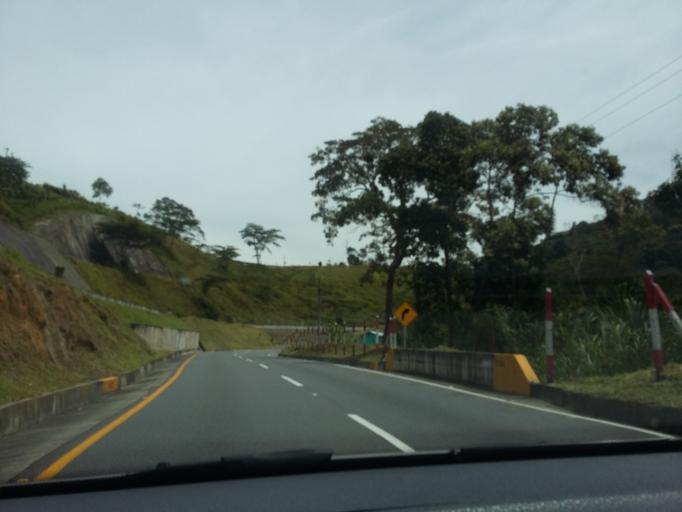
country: CO
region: Santander
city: Bucaramanga
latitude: 7.1164
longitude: -73.0789
